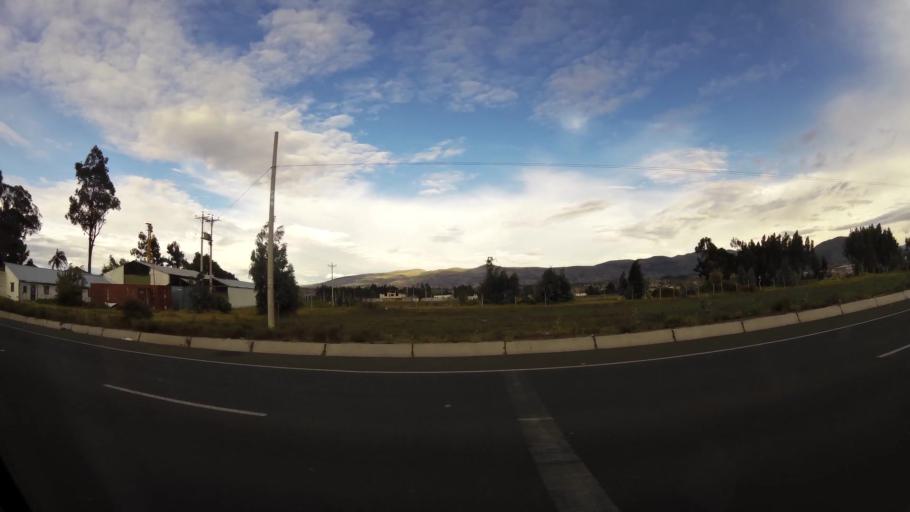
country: EC
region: Cotopaxi
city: Latacunga
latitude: -0.9090
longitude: -78.6280
